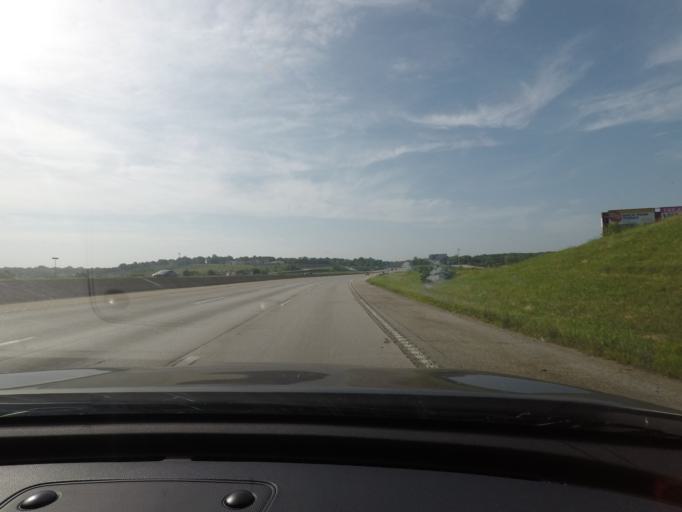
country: US
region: Missouri
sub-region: Saint Louis County
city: Bridgeton
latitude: 38.7868
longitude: -90.4205
